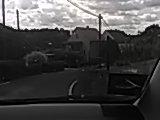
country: DE
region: Saxony
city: Meissen
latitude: 51.1966
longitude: 13.4229
